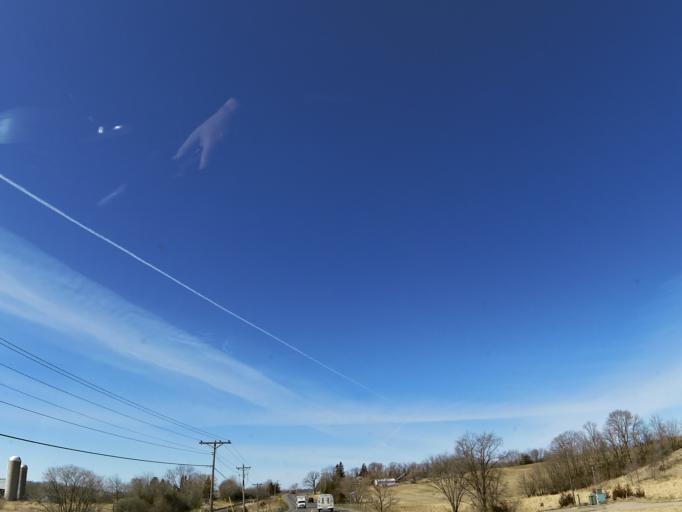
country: US
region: Minnesota
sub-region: Wright County
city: Rockford
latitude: 45.0934
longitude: -93.7558
